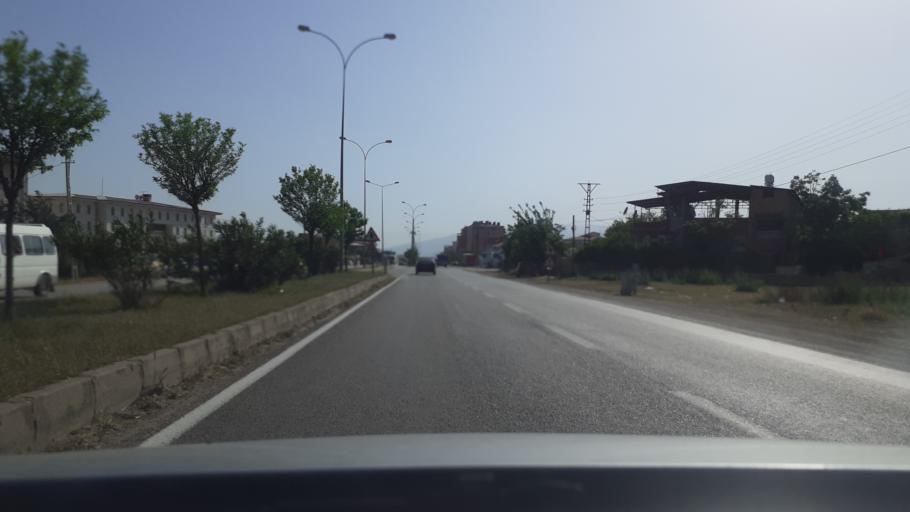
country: TR
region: Hatay
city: Kirikhan
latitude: 36.4848
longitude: 36.3627
